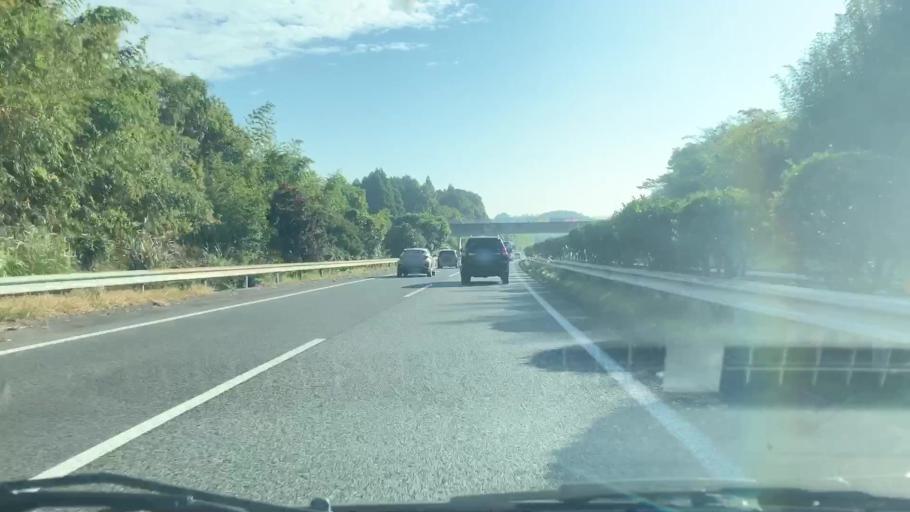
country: JP
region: Saga Prefecture
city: Saga-shi
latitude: 33.3111
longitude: 130.2149
